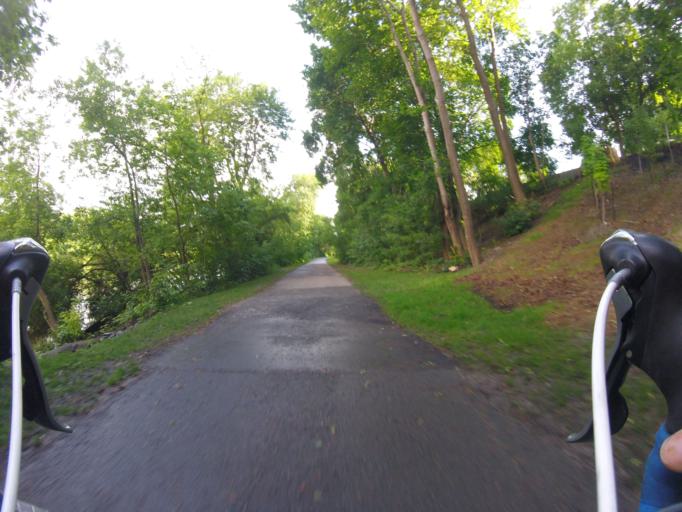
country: CA
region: Ontario
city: Ottawa
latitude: 45.4240
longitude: -75.6692
